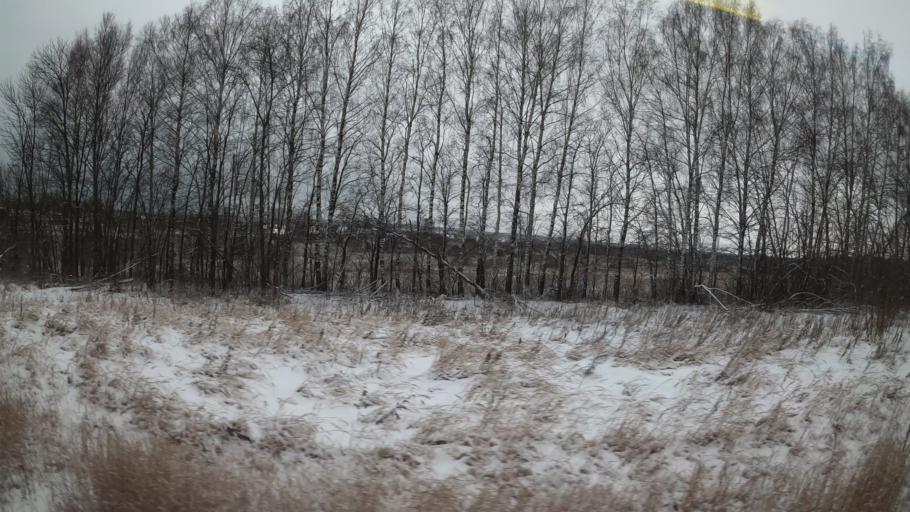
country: RU
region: Jaroslavl
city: Pereslavl'-Zalesskiy
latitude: 56.6852
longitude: 38.9199
